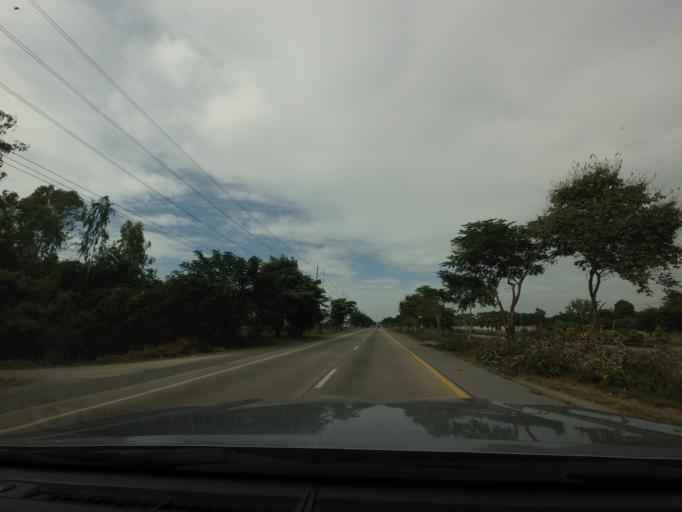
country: TH
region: Suphan Buri
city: Doem Bang Nang Buat
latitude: 14.8778
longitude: 100.0860
